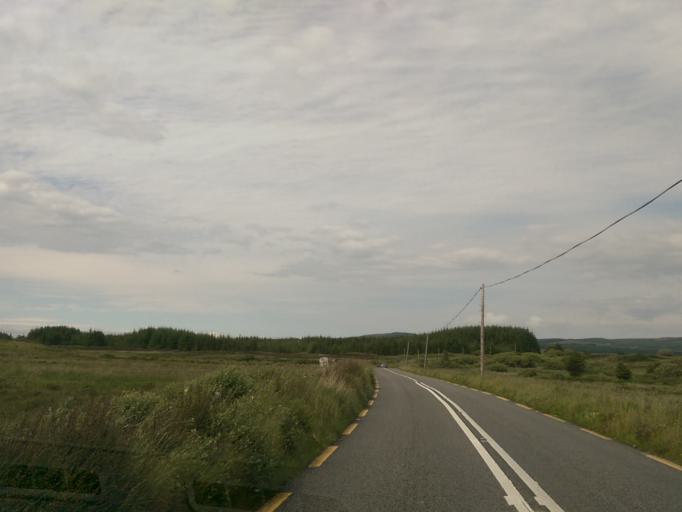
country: IE
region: Connaught
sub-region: County Galway
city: Bearna
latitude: 53.0085
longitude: -9.3131
